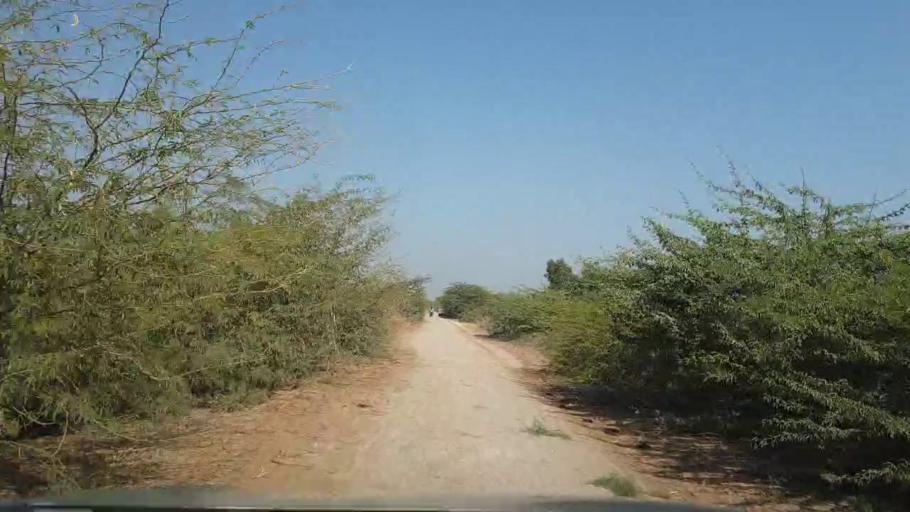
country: PK
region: Sindh
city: Berani
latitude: 25.6765
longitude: 68.8962
